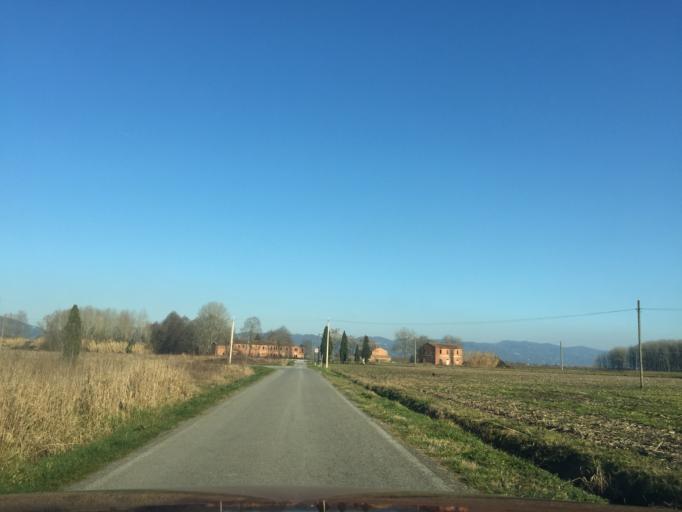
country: IT
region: Tuscany
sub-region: Provincia di Pistoia
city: Anchione
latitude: 43.8246
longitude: 10.7744
